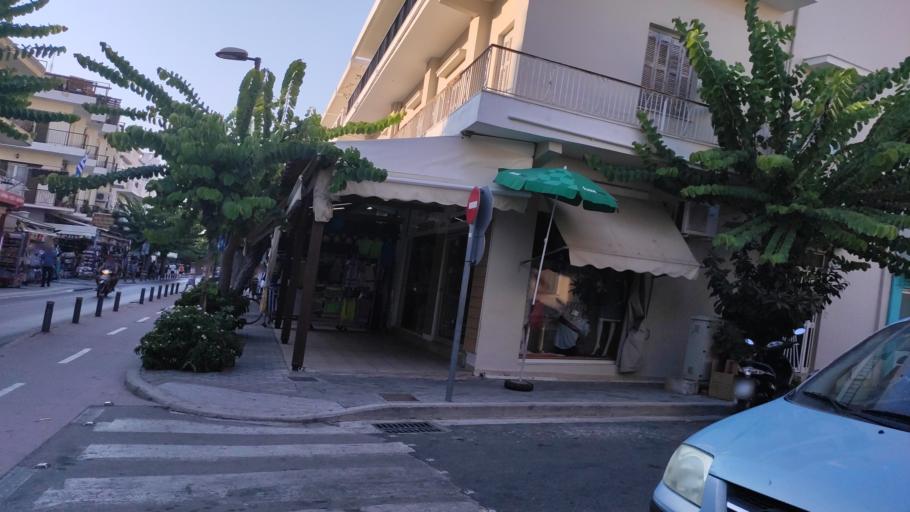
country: GR
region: South Aegean
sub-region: Nomos Dodekanisou
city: Kos
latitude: 36.8971
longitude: 27.2852
